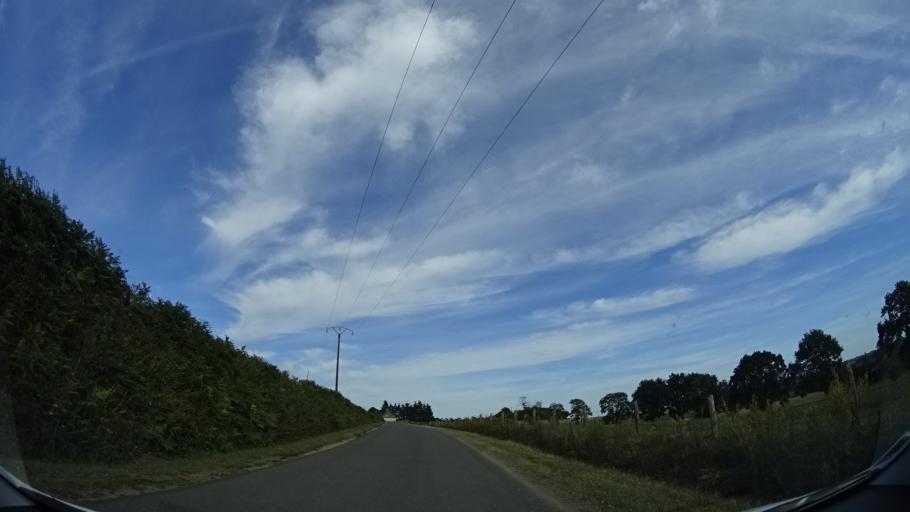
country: FR
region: Brittany
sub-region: Departement d'Ille-et-Vilaine
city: Romagne
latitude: 48.3324
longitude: -1.2553
